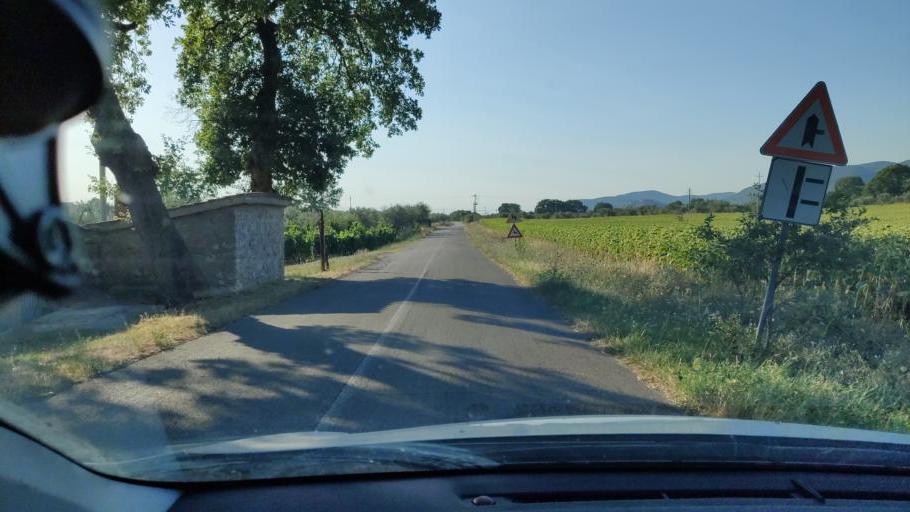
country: IT
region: Umbria
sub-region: Provincia di Terni
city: Lugnano in Teverina
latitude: 42.5468
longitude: 12.3507
